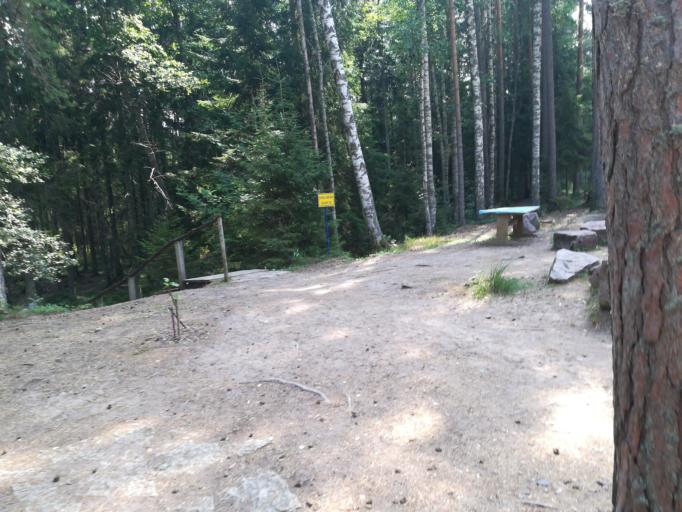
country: RU
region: Leningrad
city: Ust'-Luga
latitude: 59.7037
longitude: 28.2057
